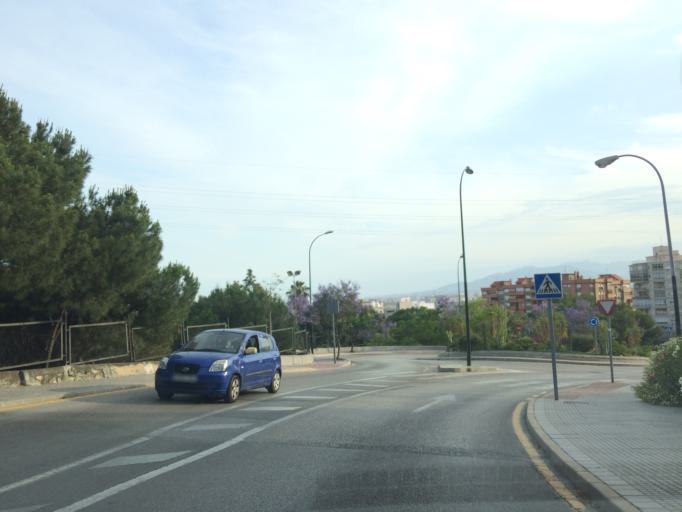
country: ES
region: Andalusia
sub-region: Provincia de Malaga
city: Malaga
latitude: 36.7372
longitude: -4.4141
